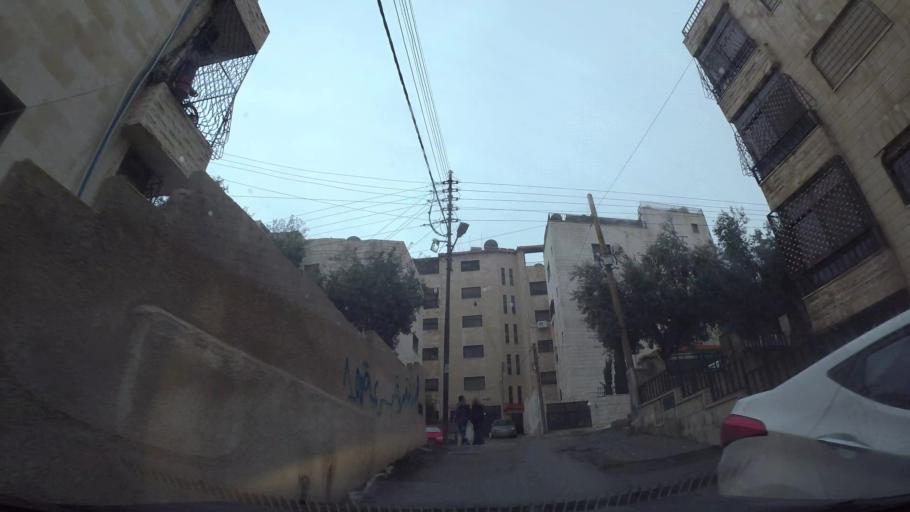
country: JO
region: Amman
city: Amman
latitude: 31.9753
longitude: 35.9174
